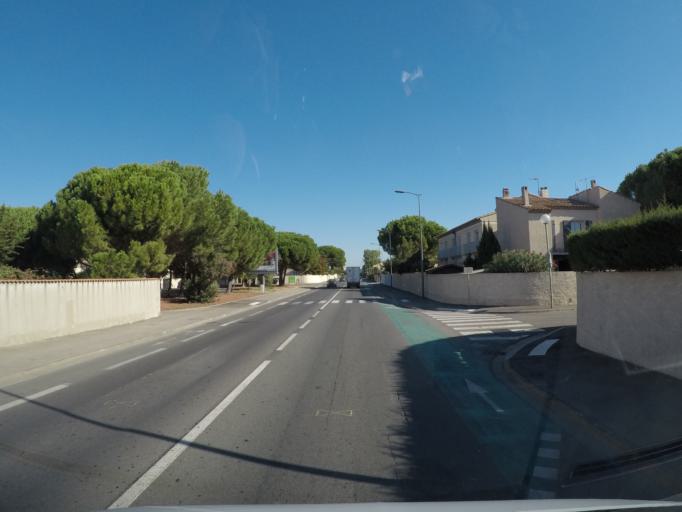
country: FR
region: Languedoc-Roussillon
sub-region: Departement de l'Aude
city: Narbonne
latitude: 43.1772
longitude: 3.0117
